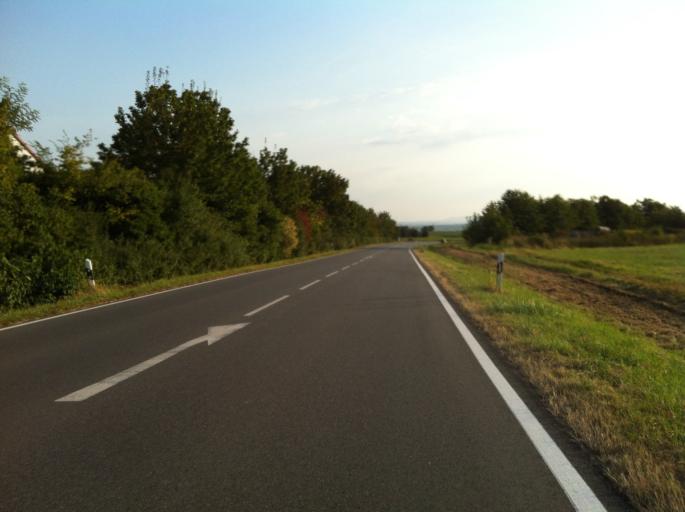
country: DE
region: Rheinland-Pfalz
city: Essenheim
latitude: 49.9299
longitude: 8.1505
